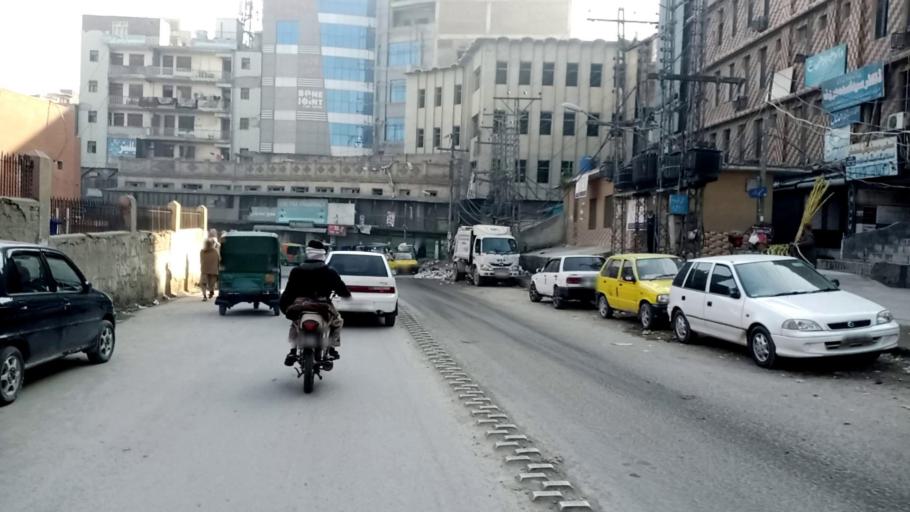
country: PK
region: Khyber Pakhtunkhwa
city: Peshawar
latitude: 34.0096
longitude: 71.5707
